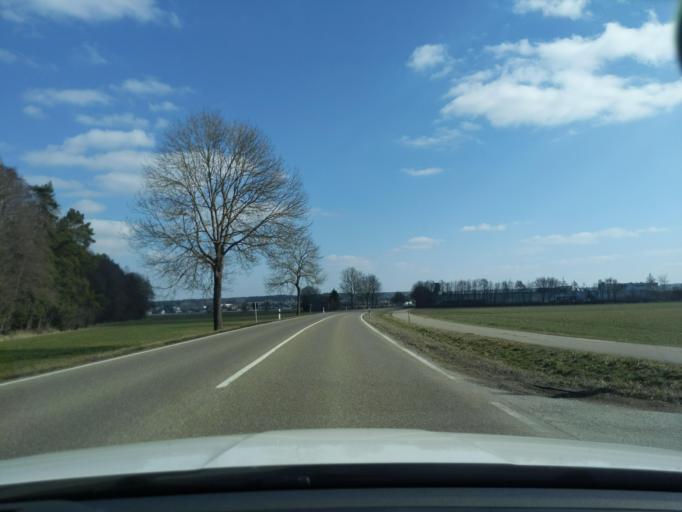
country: DE
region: Bavaria
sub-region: Swabia
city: Weissenhorn
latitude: 48.3109
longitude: 10.1351
